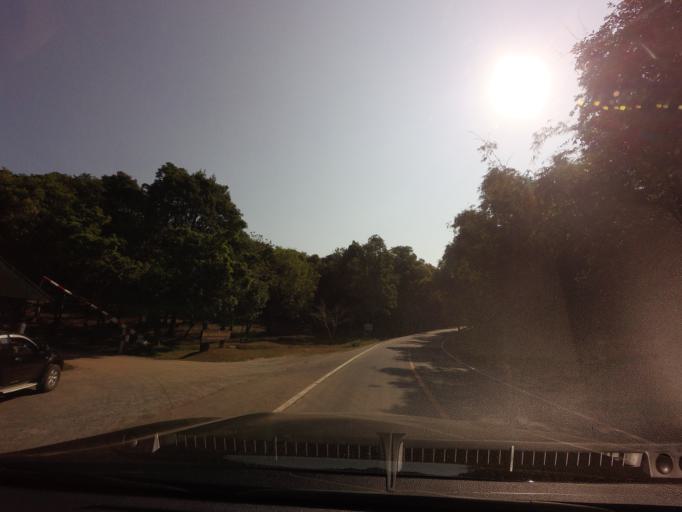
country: TH
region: Kanchanaburi
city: Thong Pha Phum
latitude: 14.6919
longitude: 98.4056
